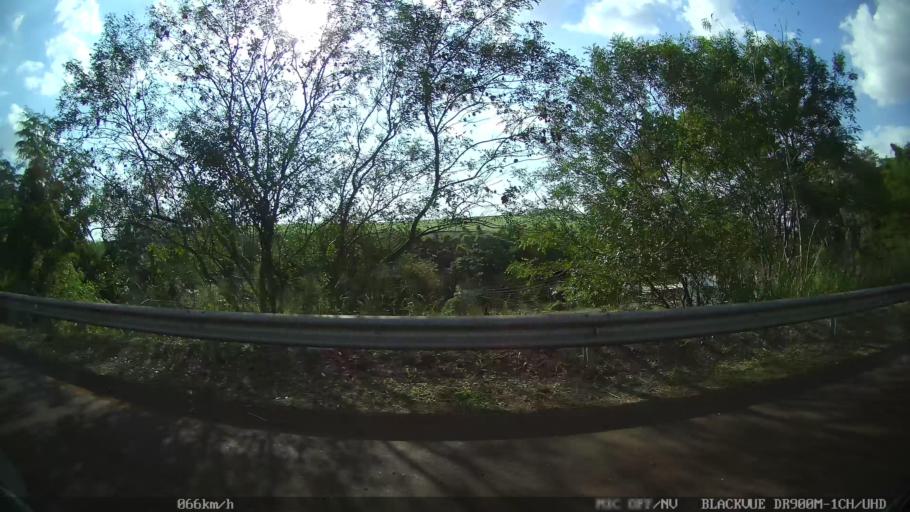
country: BR
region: Sao Paulo
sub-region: Ribeirao Preto
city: Ribeirao Preto
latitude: -21.1960
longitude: -47.8740
